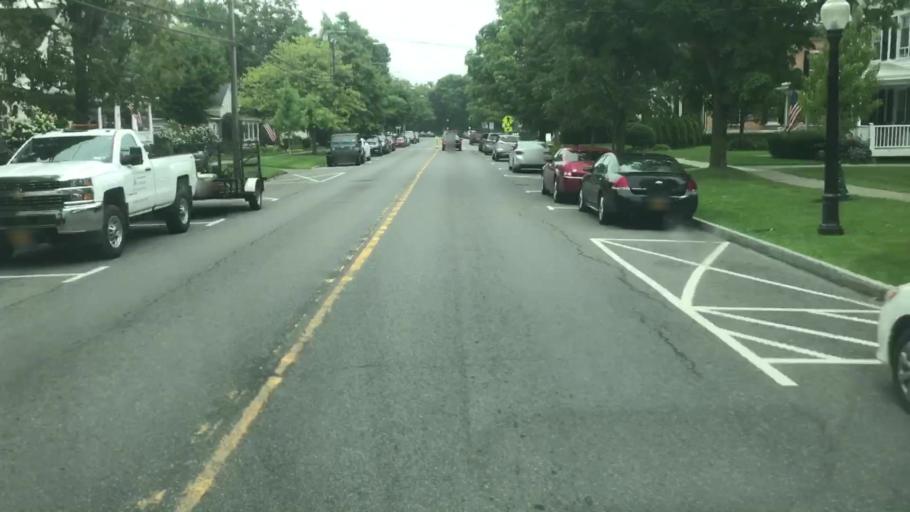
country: US
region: New York
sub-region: Onondaga County
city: Skaneateles
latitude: 42.9449
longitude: -76.4342
